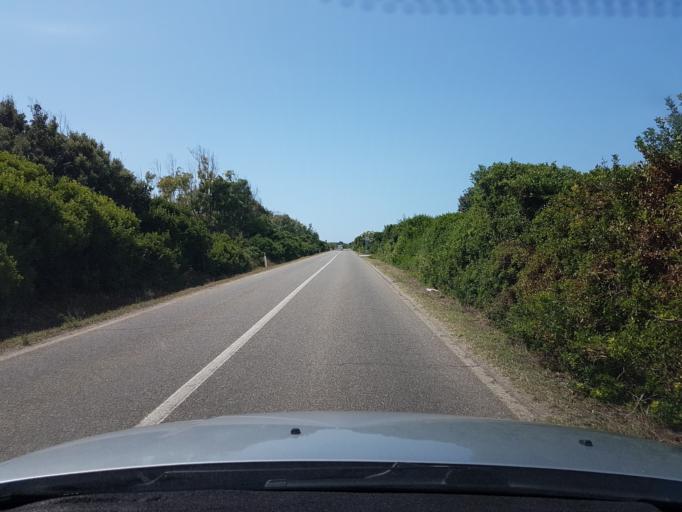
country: IT
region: Sardinia
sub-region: Provincia di Oristano
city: Riola Sardo
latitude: 40.0240
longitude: 8.4438
